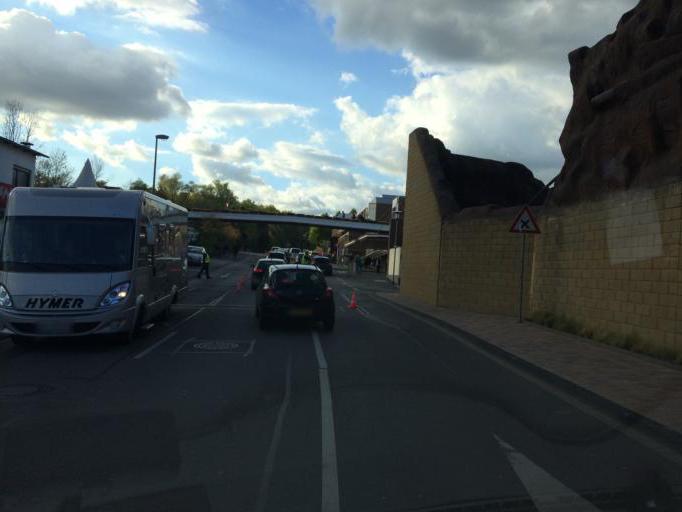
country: DE
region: North Rhine-Westphalia
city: Bruhl
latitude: 50.7984
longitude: 6.8799
